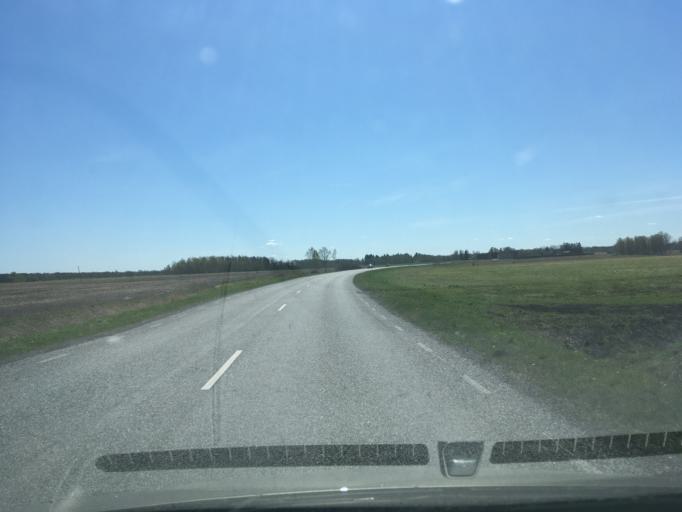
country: EE
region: Harju
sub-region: Raasiku vald
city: Arukula
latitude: 59.4193
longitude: 25.0782
